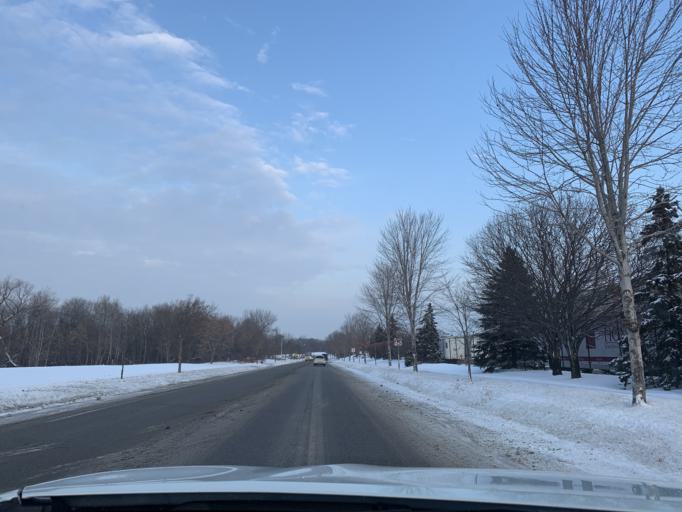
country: US
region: Minnesota
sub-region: Anoka County
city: Coon Rapids
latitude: 45.1560
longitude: -93.2817
